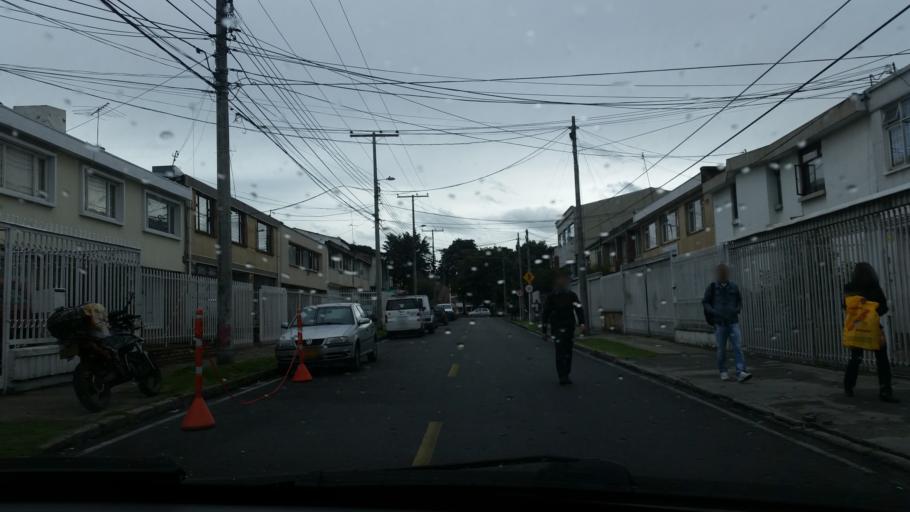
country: CO
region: Bogota D.C.
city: Barrio San Luis
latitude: 4.6811
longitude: -74.0608
